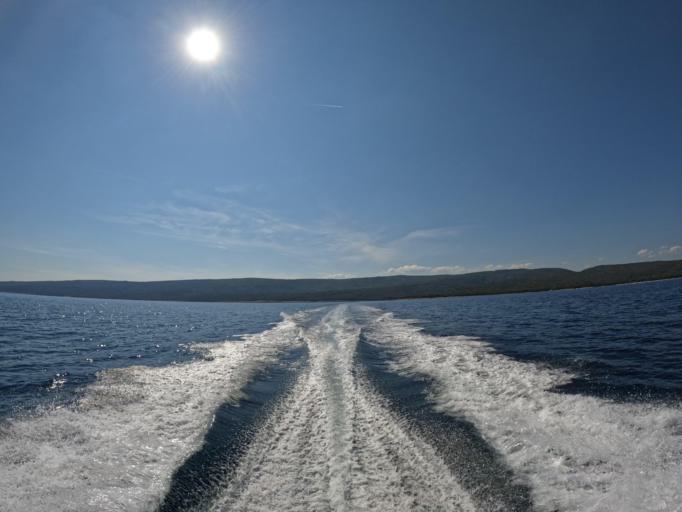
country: HR
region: Primorsko-Goranska
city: Cres
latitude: 44.9455
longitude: 14.4863
